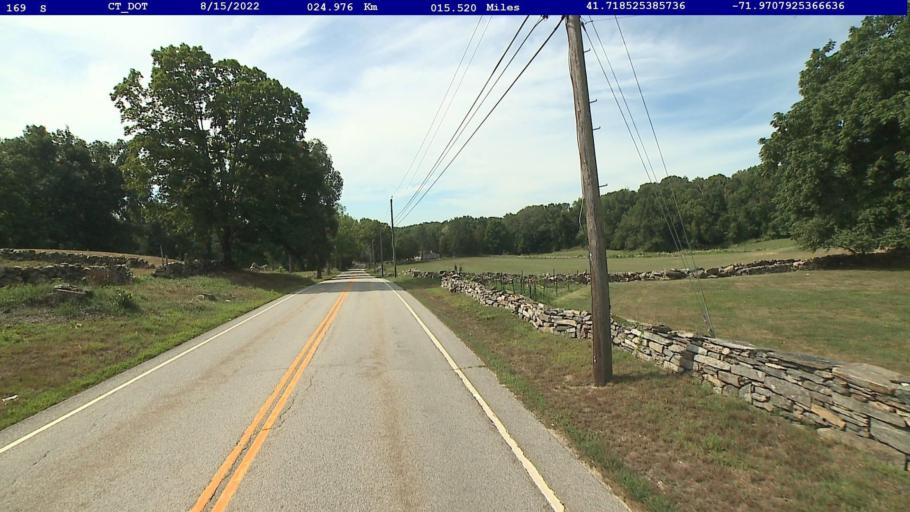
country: US
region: Connecticut
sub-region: Windham County
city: Plainfield Village
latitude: 41.7185
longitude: -71.9708
